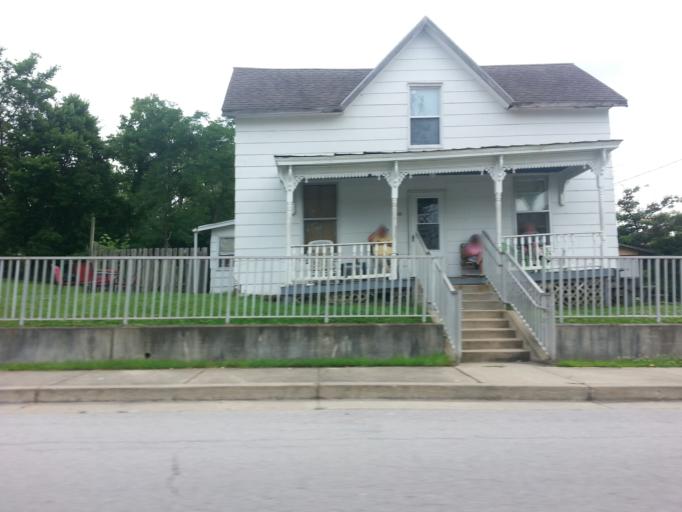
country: US
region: Kentucky
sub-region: Robertson County
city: Mount Olivet
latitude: 38.5323
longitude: -84.0401
